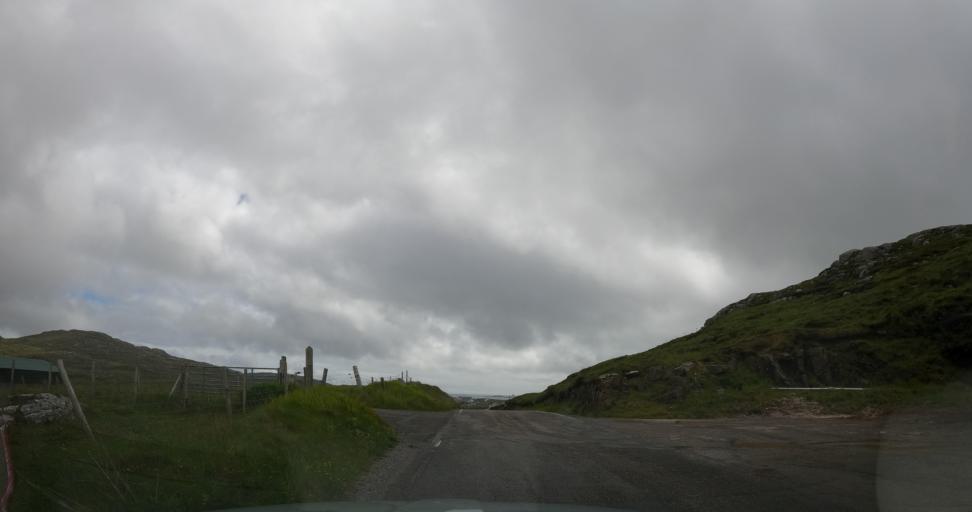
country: GB
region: Scotland
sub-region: Eilean Siar
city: Barra
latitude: 56.9621
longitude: -7.5082
